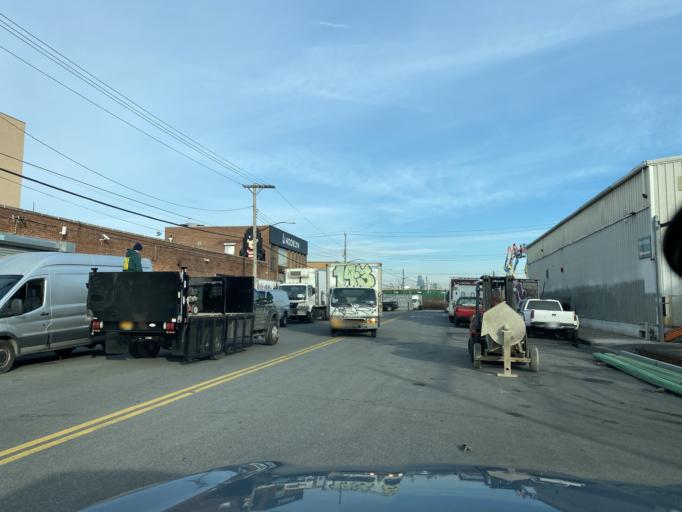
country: US
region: New York
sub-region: Queens County
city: Long Island City
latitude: 40.7094
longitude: -73.9242
